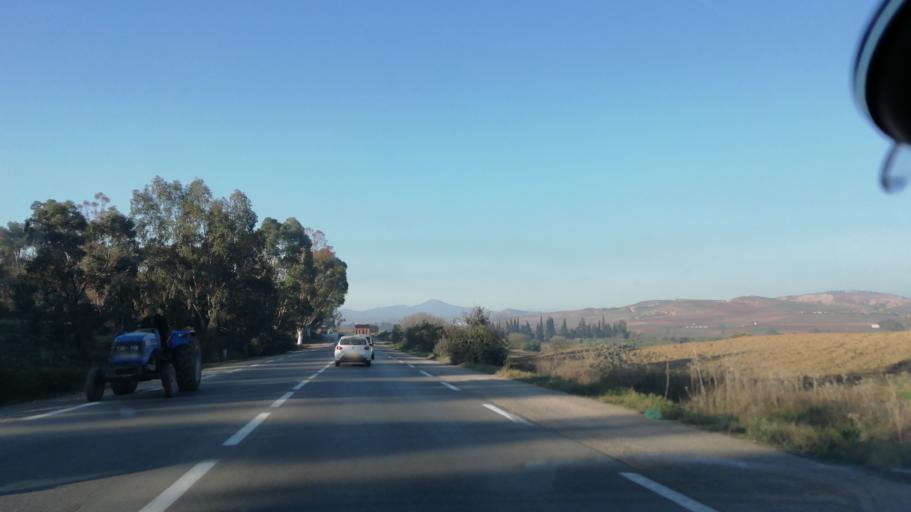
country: DZ
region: Tlemcen
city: Remchi
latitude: 35.0821
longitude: -1.4423
